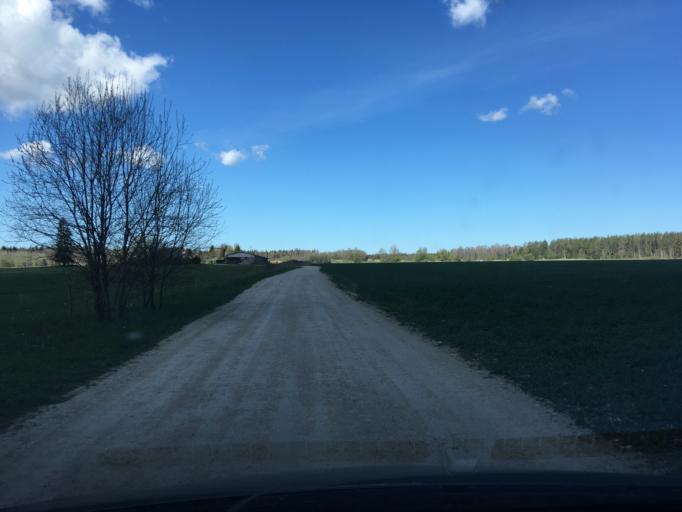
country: EE
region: Harju
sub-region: Raasiku vald
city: Raasiku
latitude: 59.2147
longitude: 25.1659
